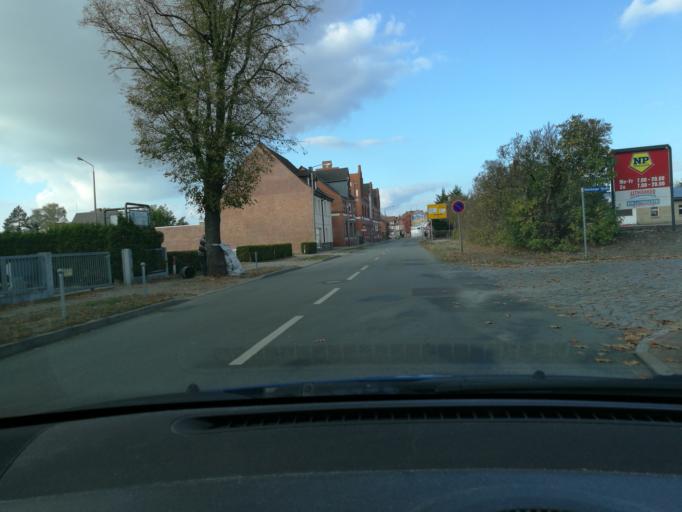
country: DE
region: Saxony-Anhalt
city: Luftkurort Arendsee
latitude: 52.8796
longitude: 11.4900
